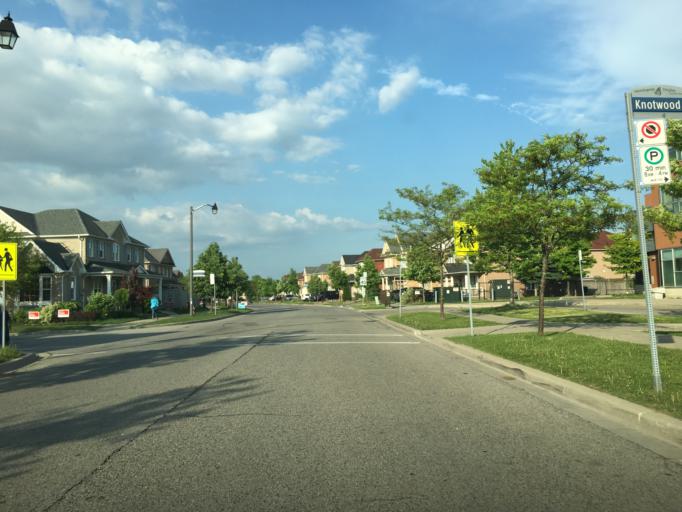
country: CA
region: Ontario
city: Markham
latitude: 43.8248
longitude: -79.2266
